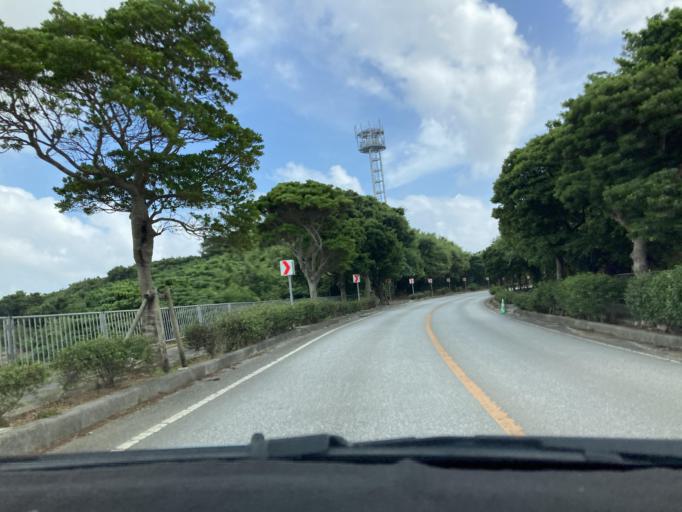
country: JP
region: Okinawa
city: Itoman
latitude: 26.1042
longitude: 127.6779
